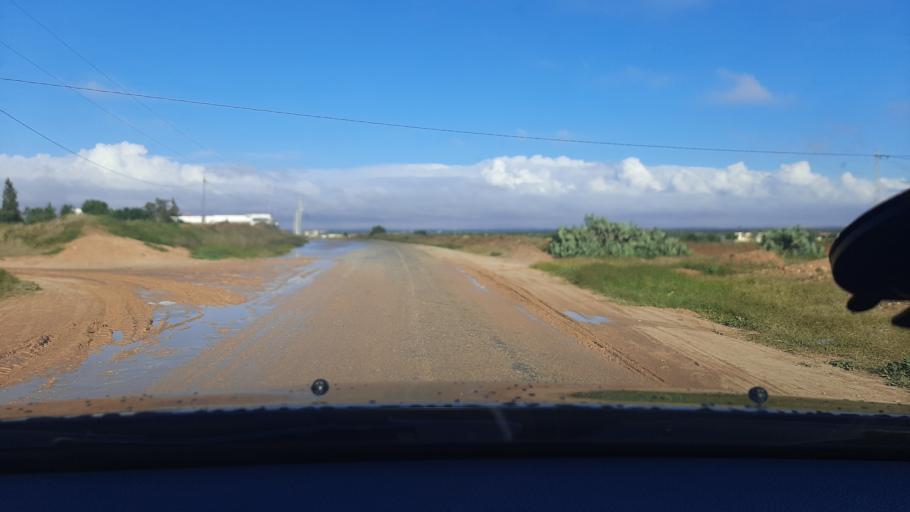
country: TN
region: Safaqis
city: Sfax
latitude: 34.8808
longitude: 10.6325
